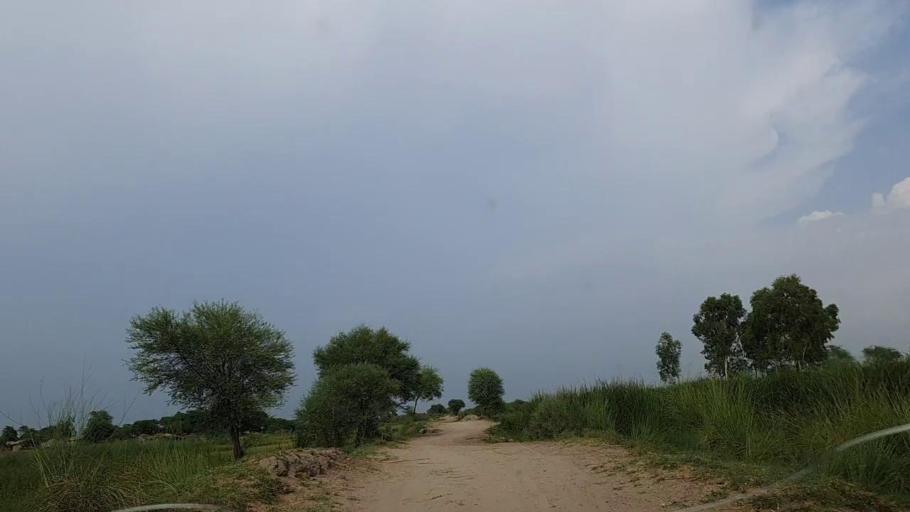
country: PK
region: Sindh
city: Khanpur
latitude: 27.8184
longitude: 69.5365
